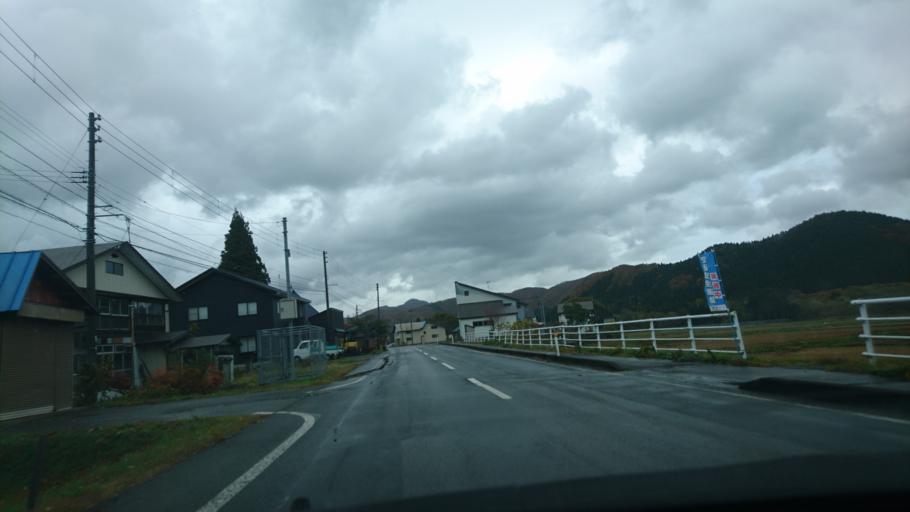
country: JP
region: Akita
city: Kakunodatemachi
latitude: 39.4883
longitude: 140.8075
